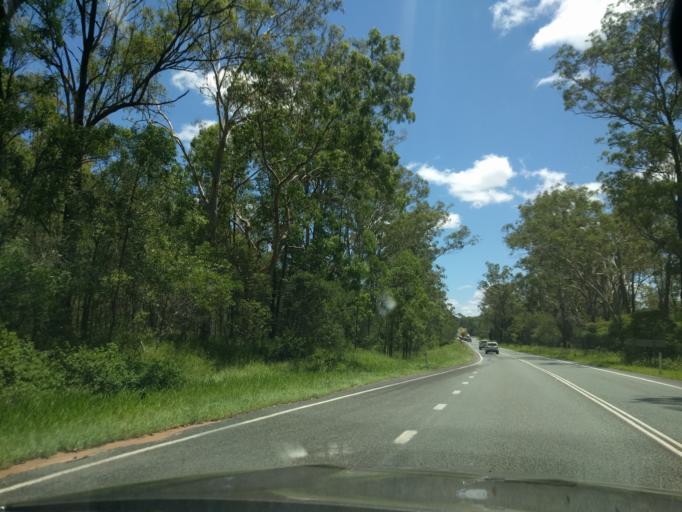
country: AU
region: Queensland
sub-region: Logan
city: Cedar Vale
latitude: -27.8478
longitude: 153.0193
